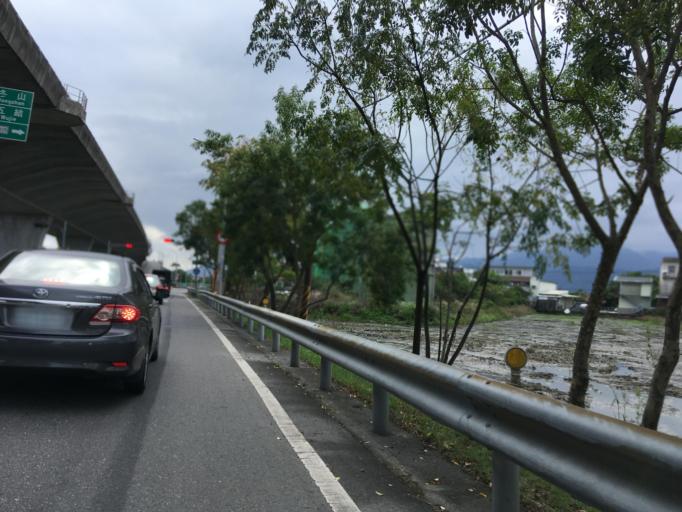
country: TW
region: Taiwan
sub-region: Yilan
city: Yilan
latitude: 24.6654
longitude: 121.7980
